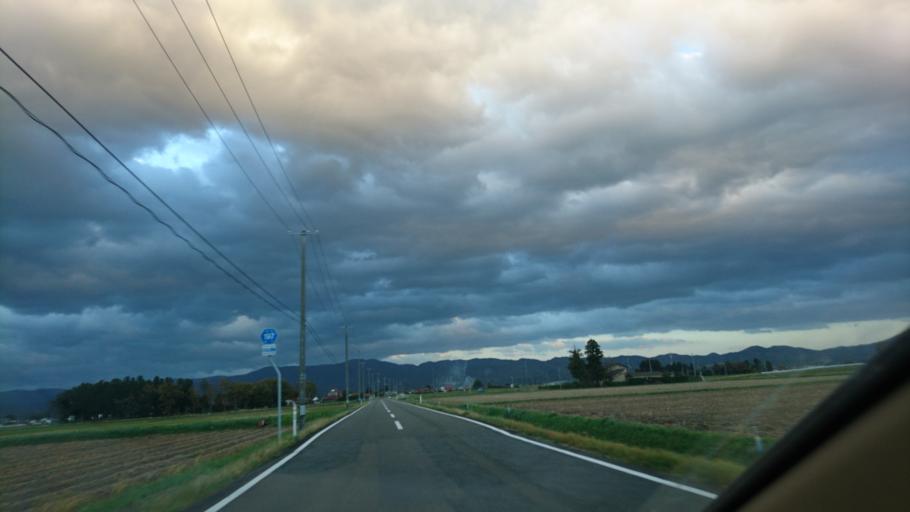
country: JP
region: Iwate
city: Mizusawa
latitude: 39.0912
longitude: 141.1436
